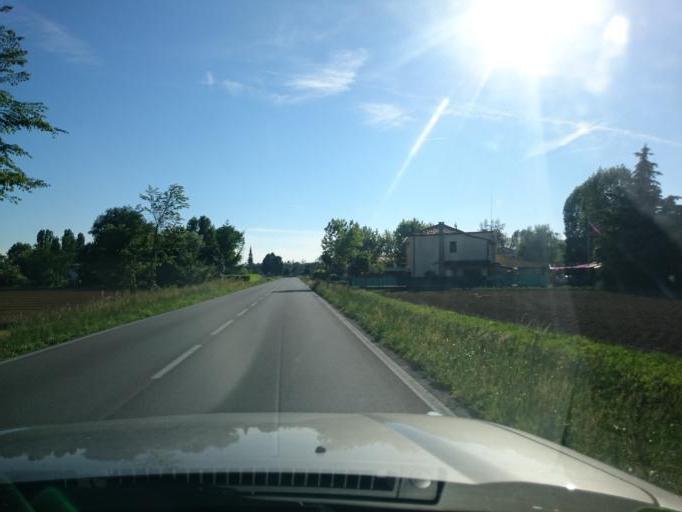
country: IT
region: Veneto
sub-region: Provincia di Venezia
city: Noale
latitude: 45.5360
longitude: 12.0553
